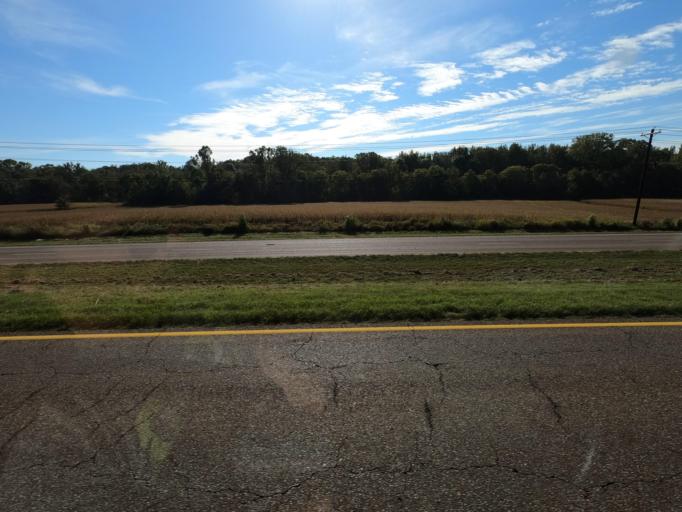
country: US
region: Tennessee
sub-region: Tipton County
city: Brighton
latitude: 35.5248
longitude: -89.6908
